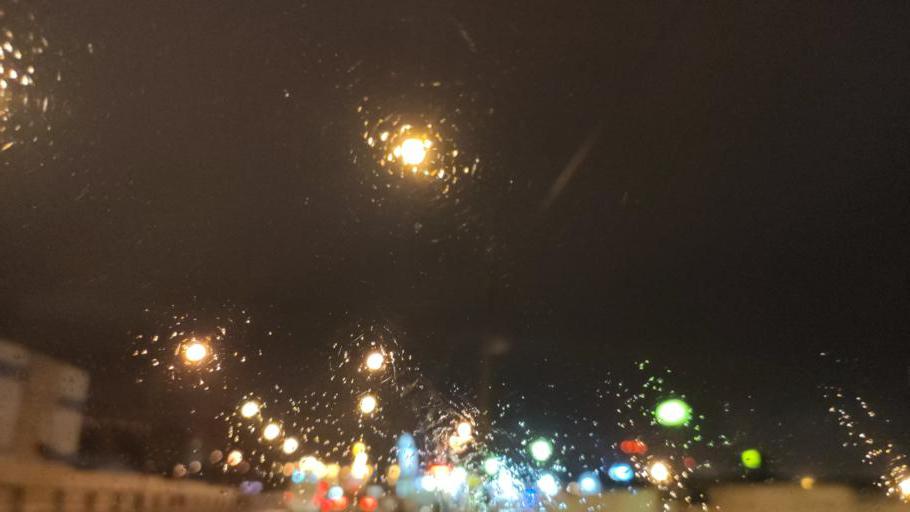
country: RU
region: Moskovskaya
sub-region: Leninskiy Rayon
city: Vnukovo
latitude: 55.6169
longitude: 37.2782
